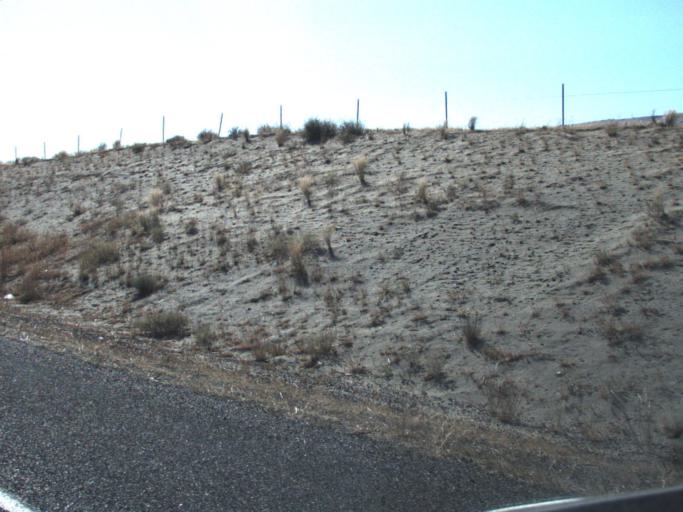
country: US
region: Washington
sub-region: Benton County
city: Benton City
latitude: 46.4958
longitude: -119.6026
